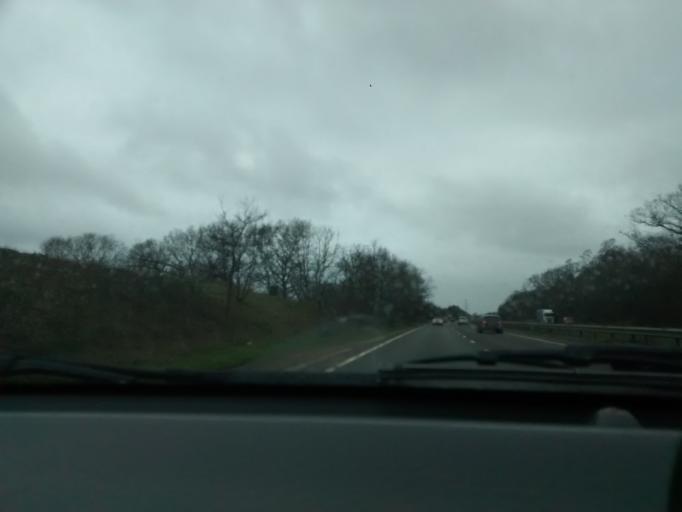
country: GB
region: England
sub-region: Suffolk
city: Needham Market
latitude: 52.1366
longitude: 1.0877
